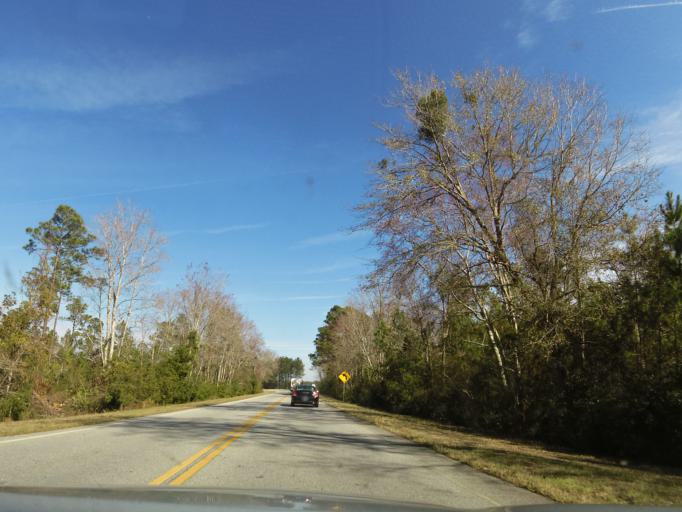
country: US
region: Georgia
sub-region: Glynn County
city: Country Club Estates
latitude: 31.2906
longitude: -81.4942
